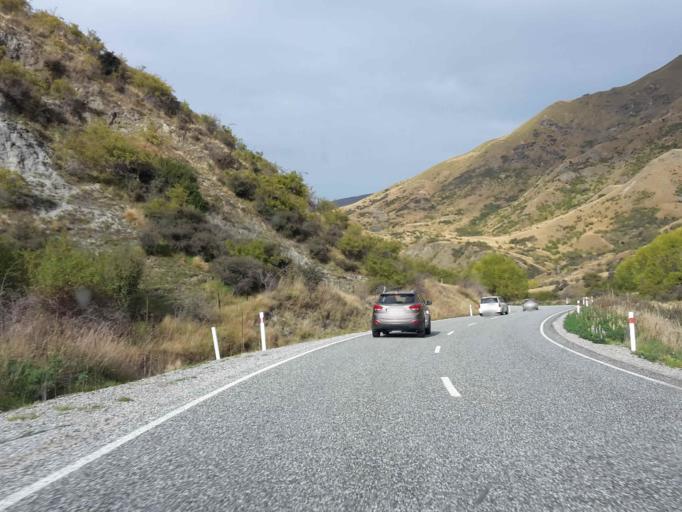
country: NZ
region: Otago
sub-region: Queenstown-Lakes District
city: Arrowtown
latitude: -44.9109
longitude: 168.9778
